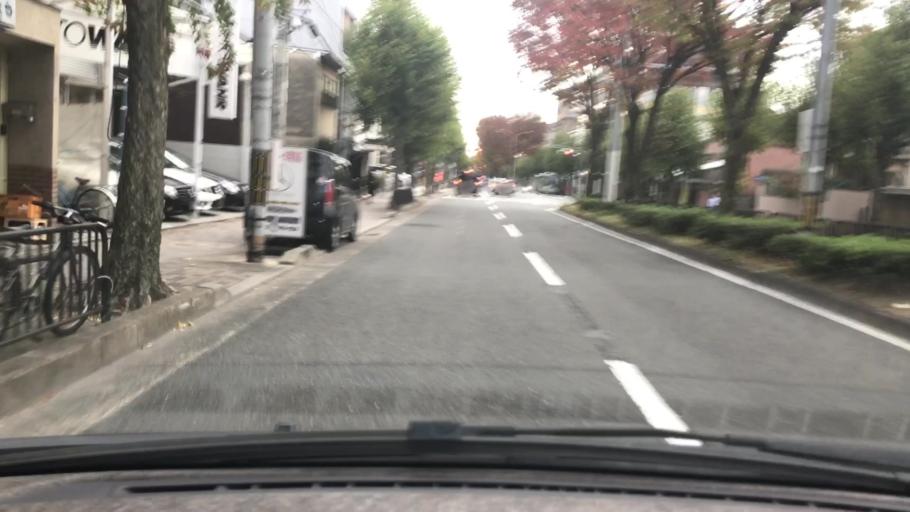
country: JP
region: Kyoto
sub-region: Kyoto-shi
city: Kamigyo-ku
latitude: 35.0491
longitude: 135.7516
